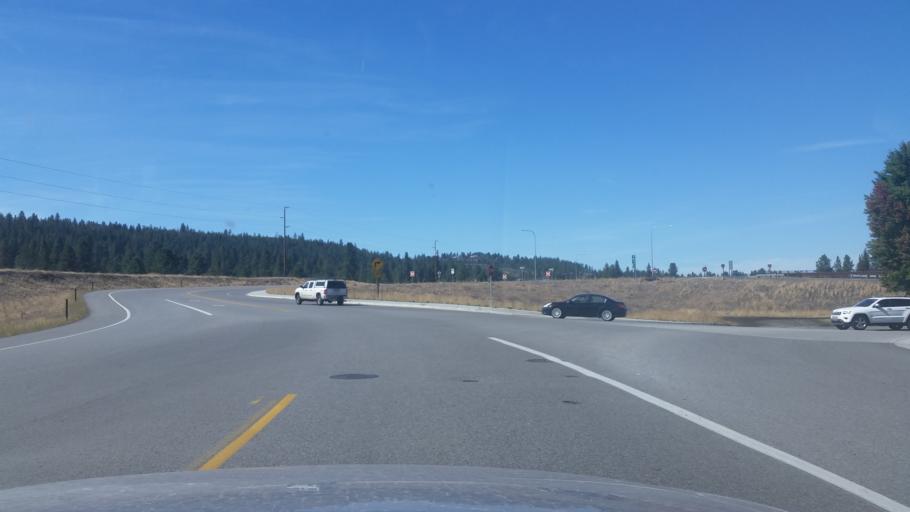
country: US
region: Washington
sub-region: Spokane County
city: Spokane
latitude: 47.6176
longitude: -117.4323
